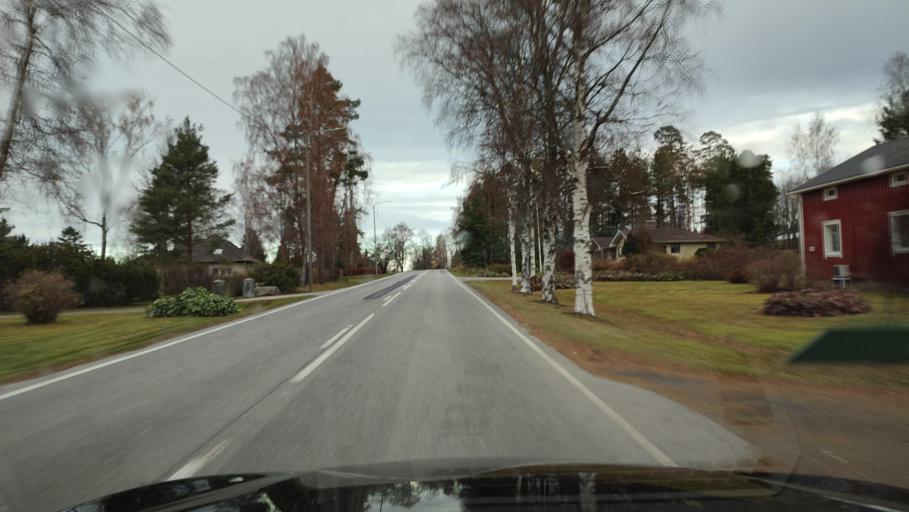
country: FI
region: Ostrobothnia
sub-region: Sydosterbotten
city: Naerpes
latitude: 62.4208
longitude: 21.3427
